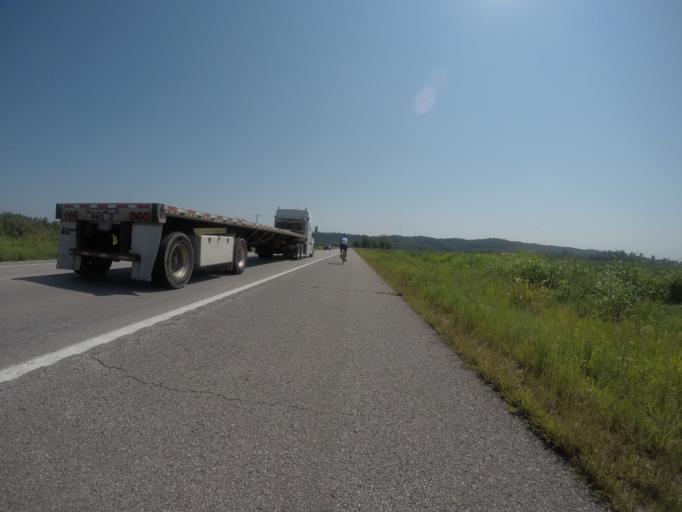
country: US
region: Kansas
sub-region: Atchison County
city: Atchison
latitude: 39.5566
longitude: -95.0619
